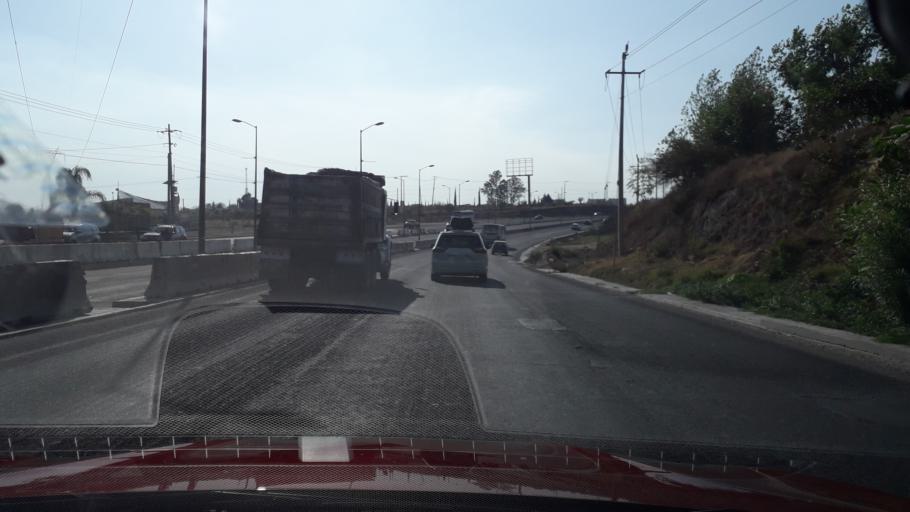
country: MX
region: Puebla
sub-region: Puebla
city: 18 de Marzo
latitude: 18.9728
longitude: -98.2075
